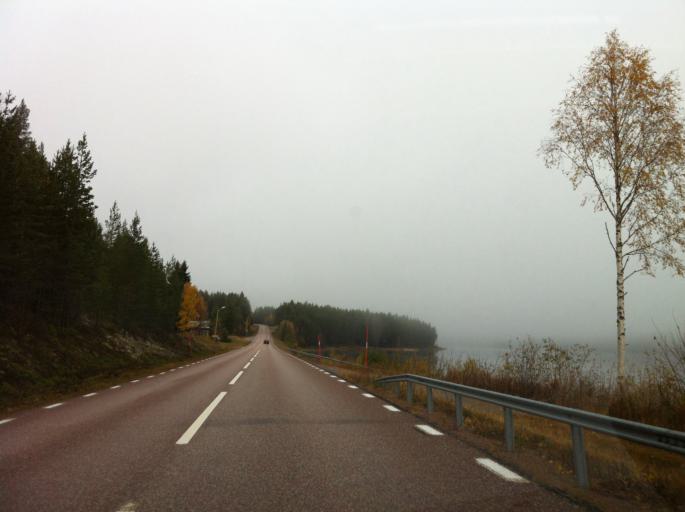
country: NO
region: Hedmark
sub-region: Trysil
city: Innbygda
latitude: 61.7403
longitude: 12.9781
